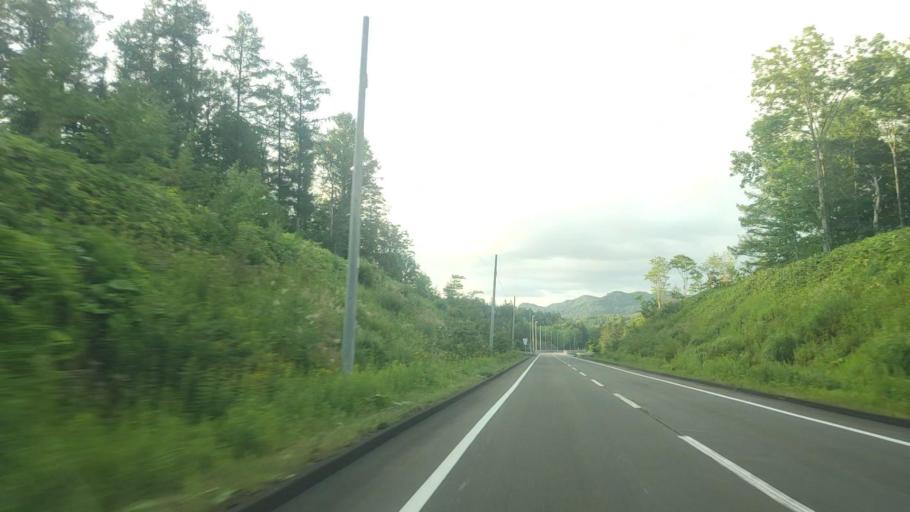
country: JP
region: Hokkaido
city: Bibai
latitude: 43.1057
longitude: 142.0978
